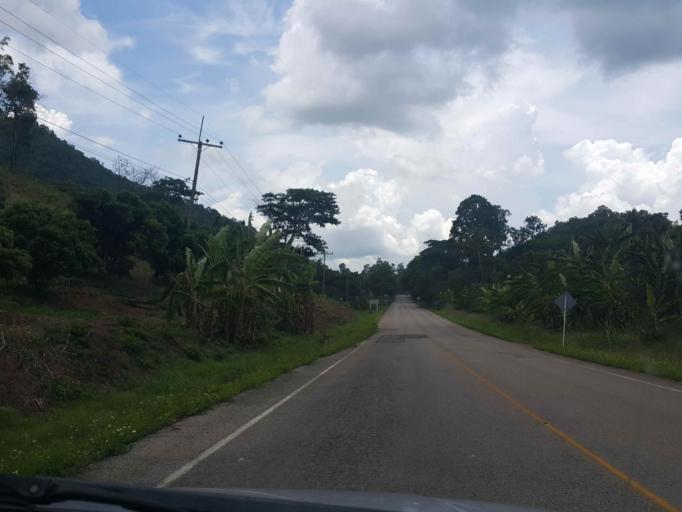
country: TH
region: Phayao
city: Chiang Muan
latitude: 18.9234
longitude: 100.1028
